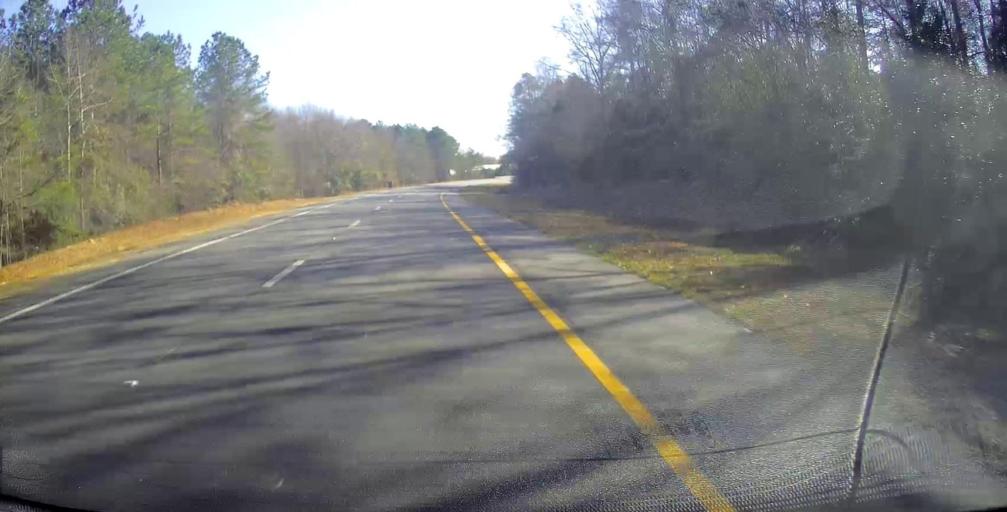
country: US
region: Georgia
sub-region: Taylor County
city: Butler
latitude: 32.5615
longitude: -84.2374
